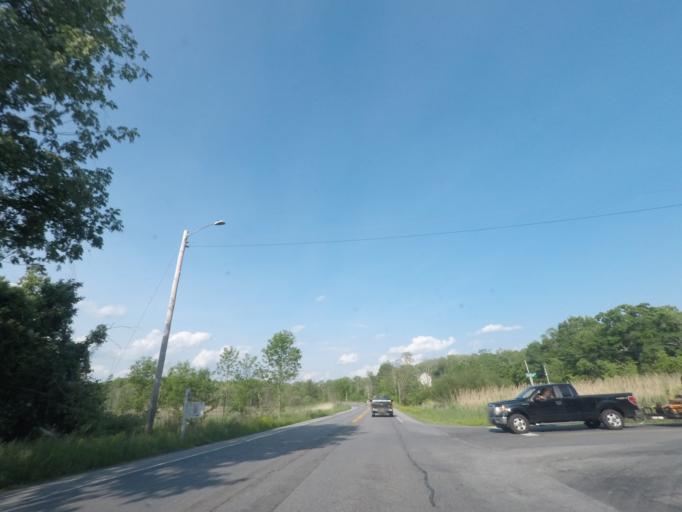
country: US
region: New York
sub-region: Orange County
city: Beaverdam Lake-Salisbury Mills
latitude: 41.4787
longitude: -74.1237
